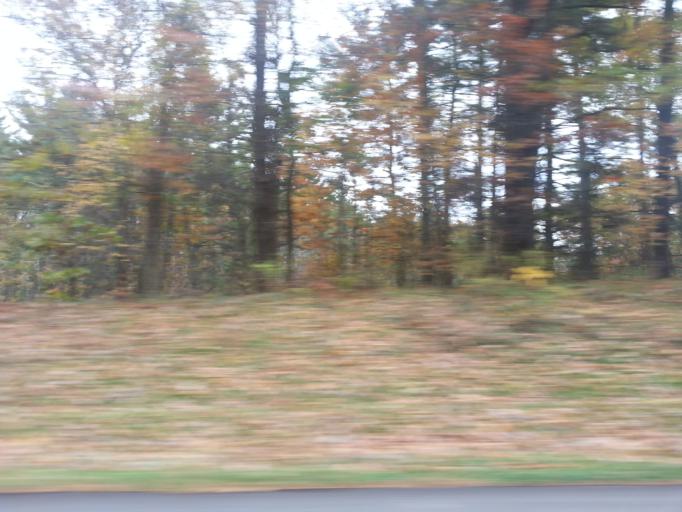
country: US
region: North Carolina
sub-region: Ashe County
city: Jefferson
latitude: 36.3339
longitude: -81.3746
